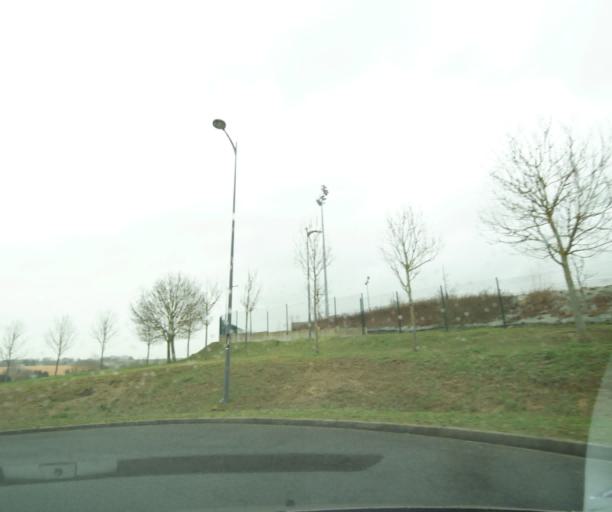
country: FR
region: Picardie
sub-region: Departement de l'Oise
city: Noyon
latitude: 49.5864
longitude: 3.0154
